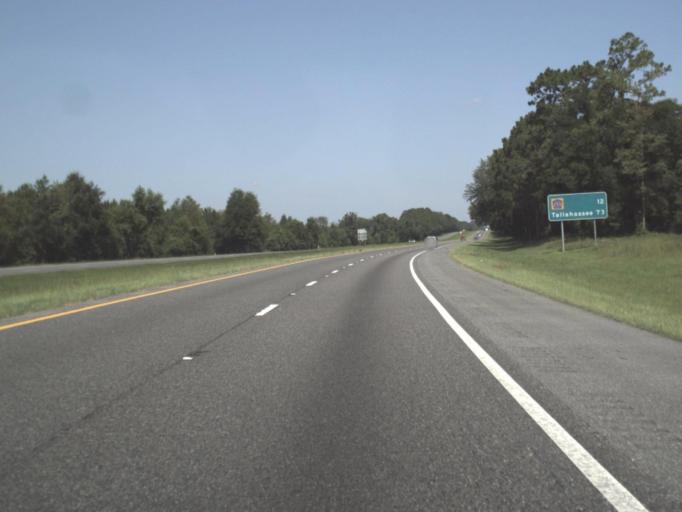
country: US
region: Florida
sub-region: Suwannee County
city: Live Oak
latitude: 30.3374
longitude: -83.1070
